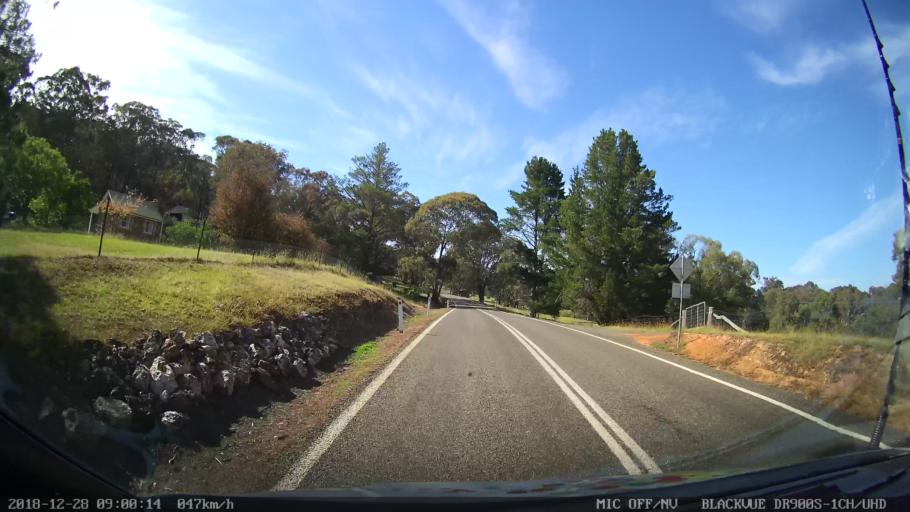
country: AU
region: New South Wales
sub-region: Upper Lachlan Shire
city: Crookwell
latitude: -34.1366
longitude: 149.3344
